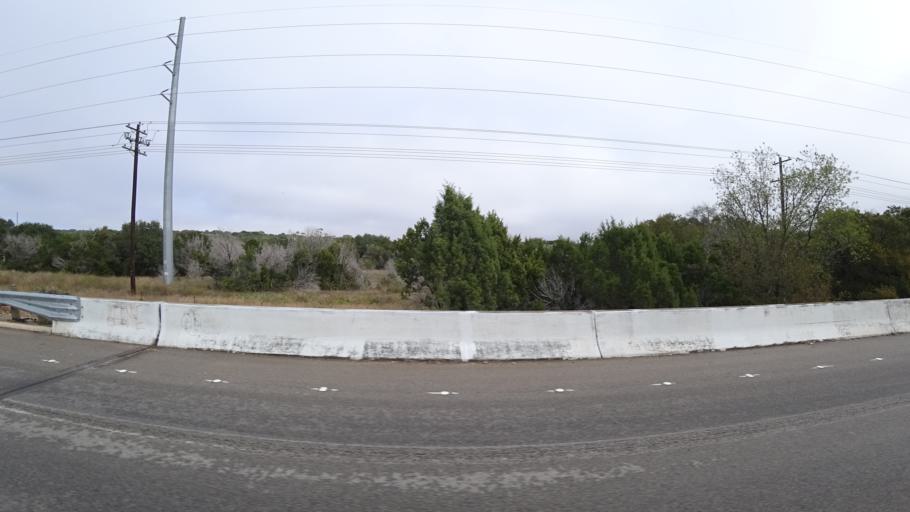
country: US
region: Texas
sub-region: Travis County
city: Shady Hollow
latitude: 30.1780
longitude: -97.8933
